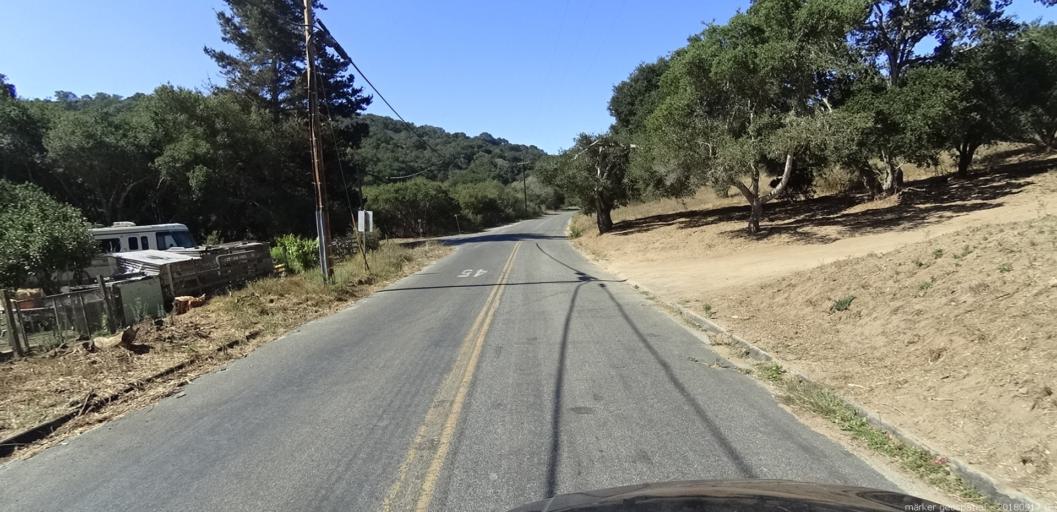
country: US
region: California
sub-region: Monterey County
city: Elkhorn
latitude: 36.8277
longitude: -121.7081
